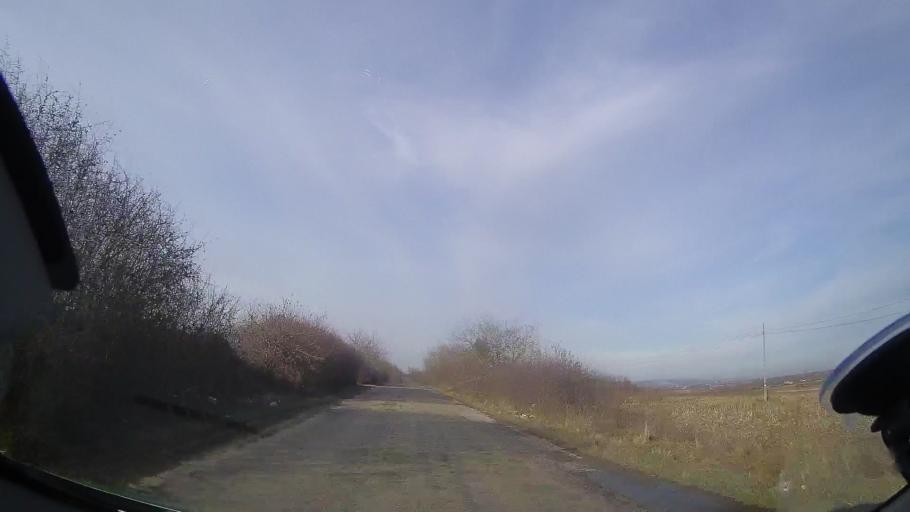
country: RO
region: Bihor
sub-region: Comuna Spinus
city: Spinus
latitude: 47.2100
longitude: 22.1794
